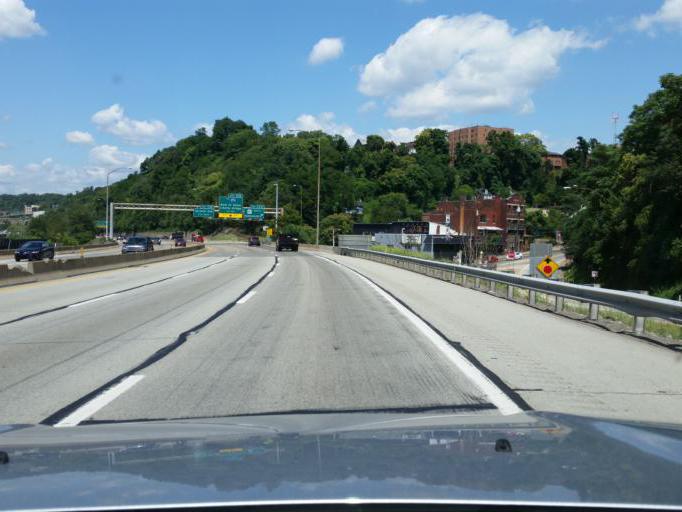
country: US
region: Pennsylvania
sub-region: Allegheny County
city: Bloomfield
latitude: 40.4308
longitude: -79.9578
